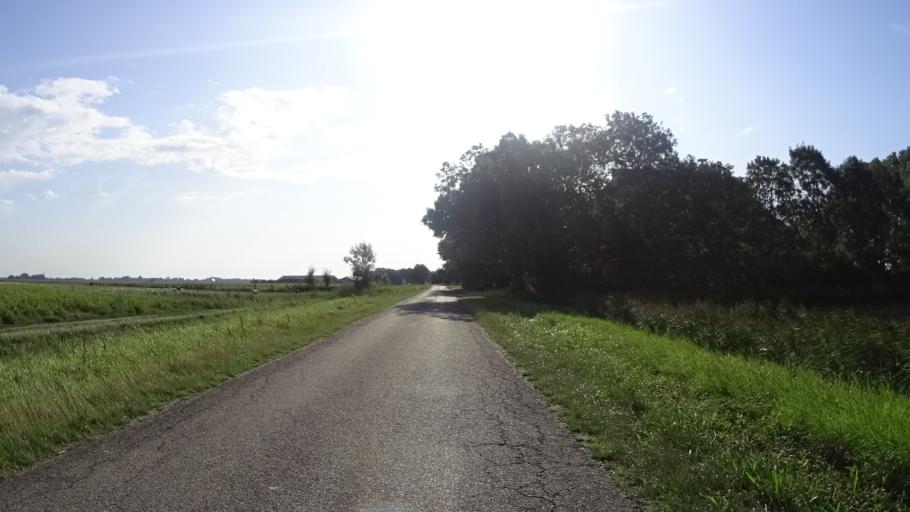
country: NL
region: Friesland
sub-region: Gemeente Harlingen
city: Harlingen
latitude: 53.1230
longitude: 5.4379
